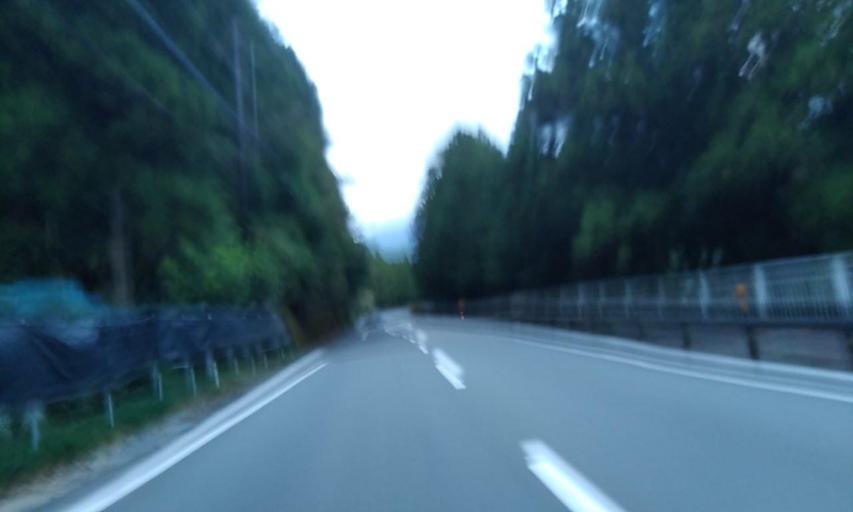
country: JP
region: Wakayama
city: Shingu
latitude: 33.7372
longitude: 135.9396
